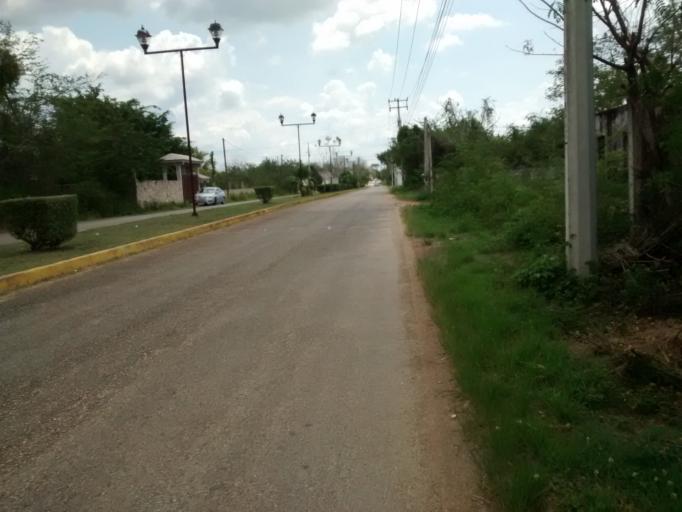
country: MX
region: Yucatan
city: Valladolid
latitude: 20.6868
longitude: -88.2214
